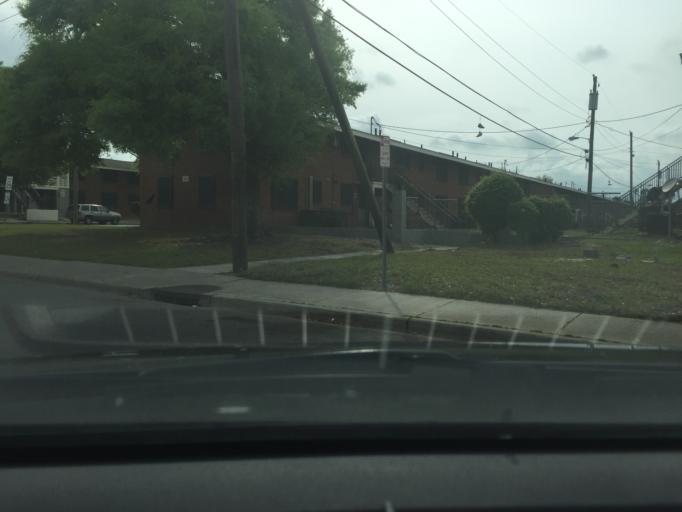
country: US
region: Georgia
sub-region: Chatham County
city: Savannah
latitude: 32.0698
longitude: -81.1022
